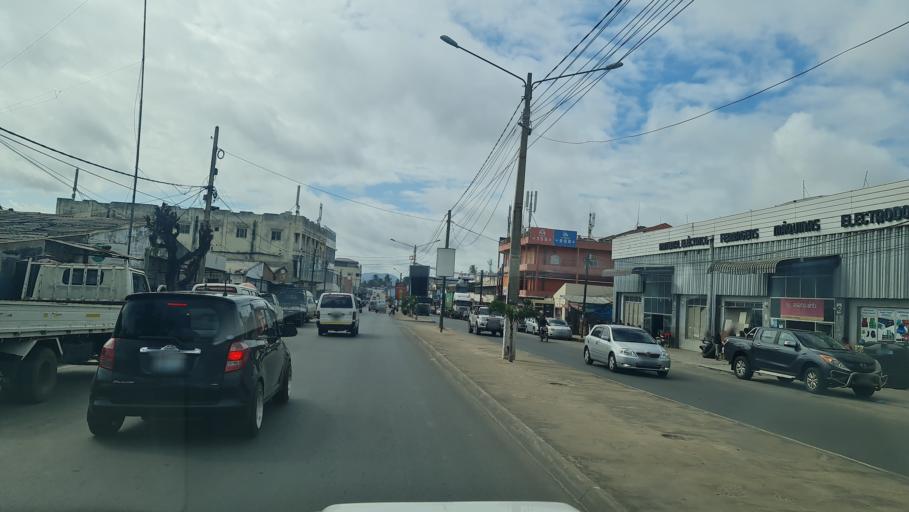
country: MZ
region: Nampula
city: Nampula
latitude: -15.1146
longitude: 39.2765
